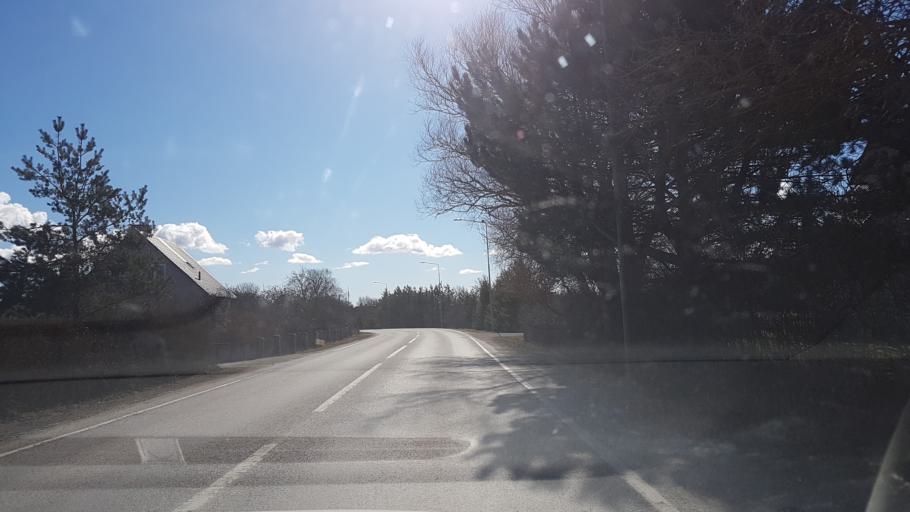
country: SE
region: Gotland
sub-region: Gotland
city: Visby
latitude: 57.5193
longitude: 18.4430
